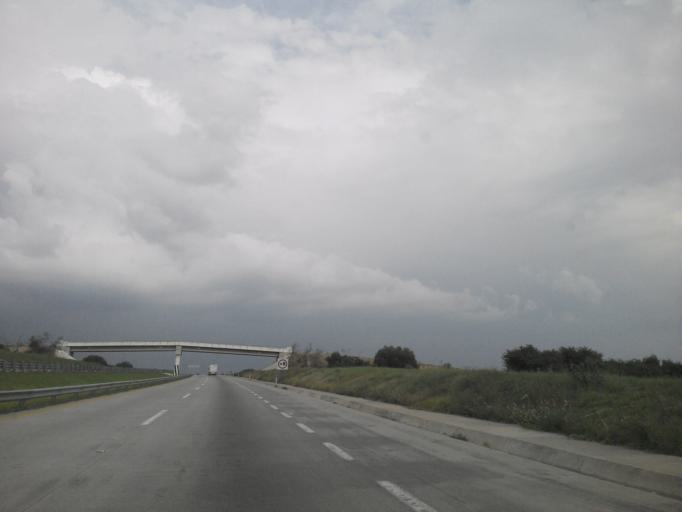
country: MX
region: Mexico
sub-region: Apaxco
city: Colonia Juarez
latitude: 19.9746
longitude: -99.1096
